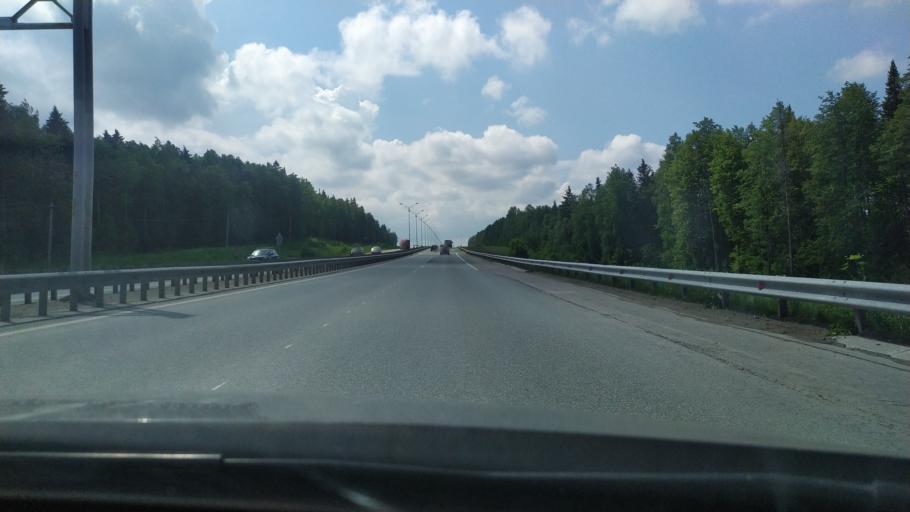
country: RU
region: Perm
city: Ferma
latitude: 58.0095
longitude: 56.3986
